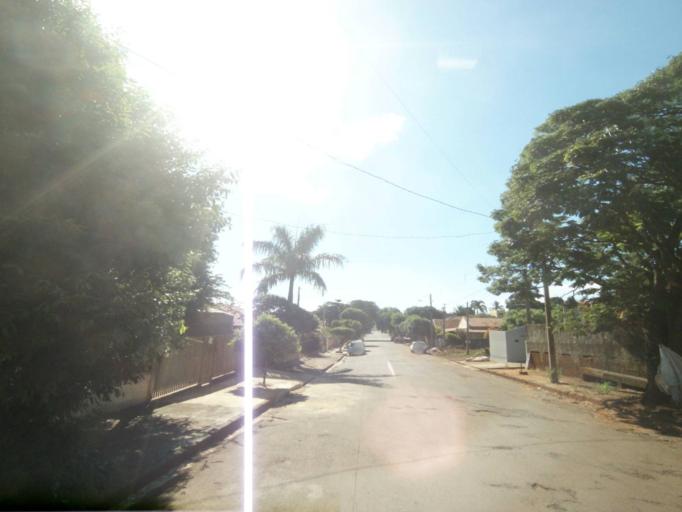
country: BR
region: Parana
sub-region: Sertanopolis
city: Sertanopolis
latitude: -23.0346
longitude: -50.8197
